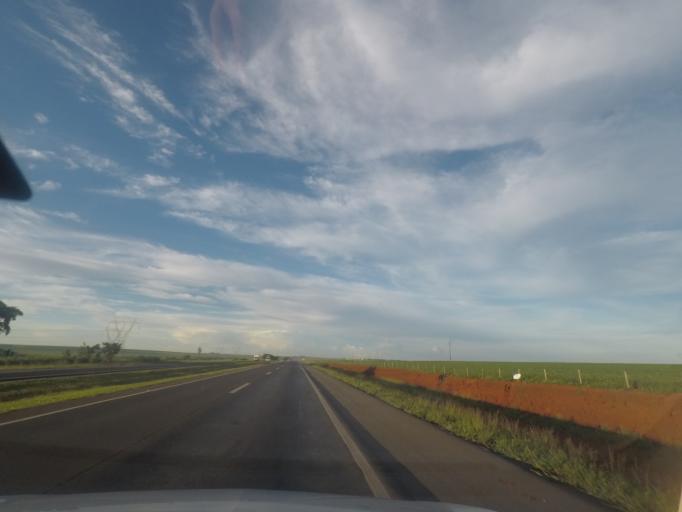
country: BR
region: Goias
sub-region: Goiatuba
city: Goiatuba
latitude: -17.9695
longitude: -49.2538
